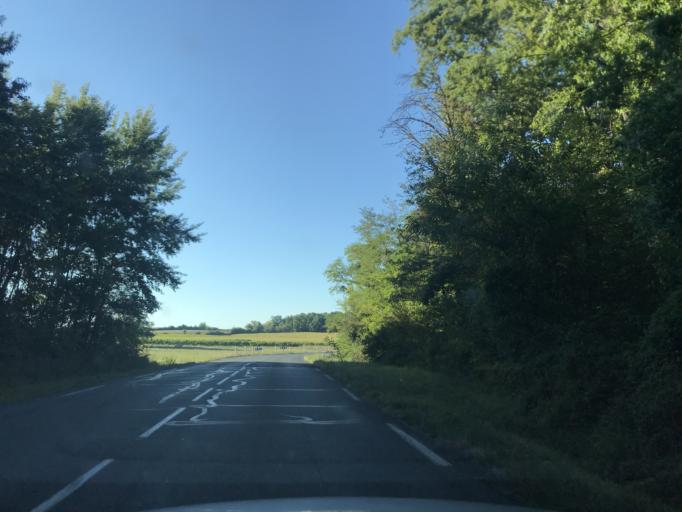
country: FR
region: Aquitaine
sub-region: Departement de la Gironde
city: Sauveterre-de-Guyenne
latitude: 44.6700
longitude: -0.1030
